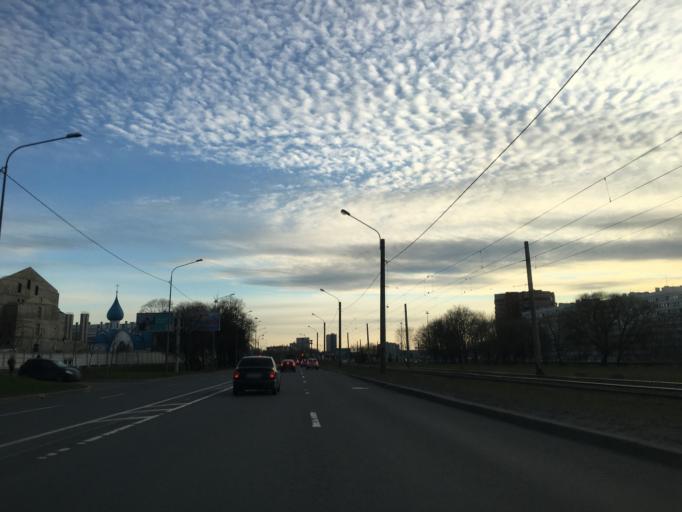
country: RU
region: St.-Petersburg
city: Dachnoye
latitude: 59.8537
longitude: 30.2419
